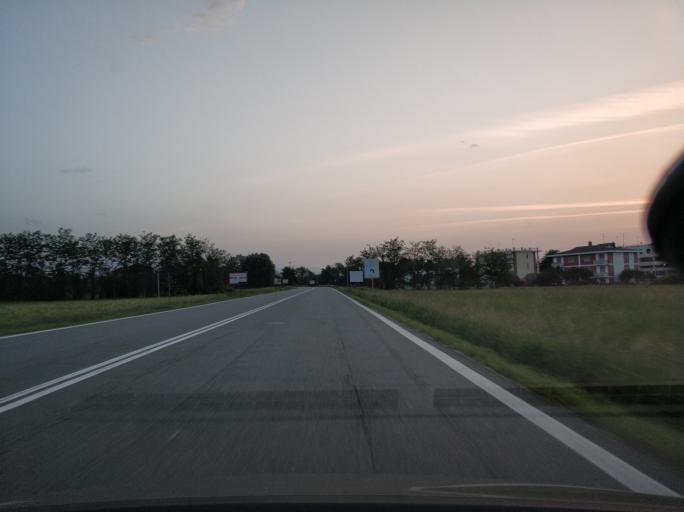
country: IT
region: Piedmont
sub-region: Provincia di Torino
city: Caselle Torinese
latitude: 45.1911
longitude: 7.6398
